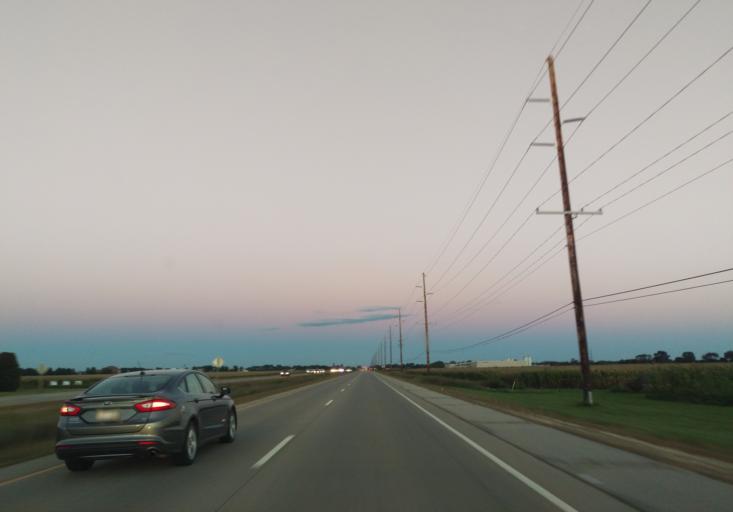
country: US
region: Wisconsin
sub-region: Rock County
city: Janesville
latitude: 42.7282
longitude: -89.0256
